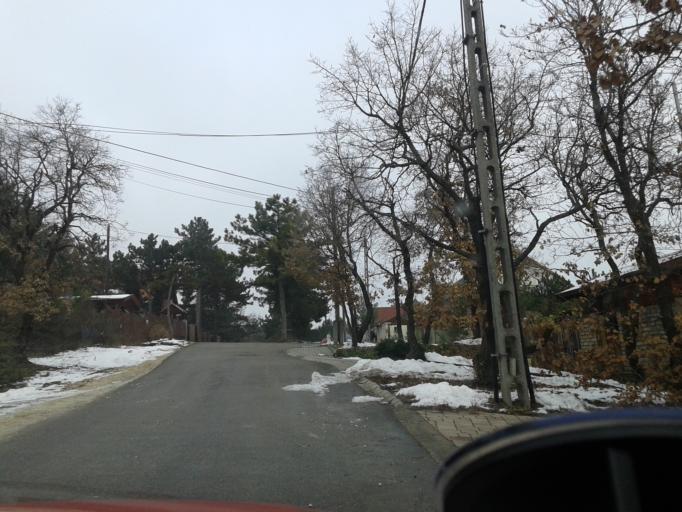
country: HU
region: Pest
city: Erd
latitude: 47.4036
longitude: 18.9299
